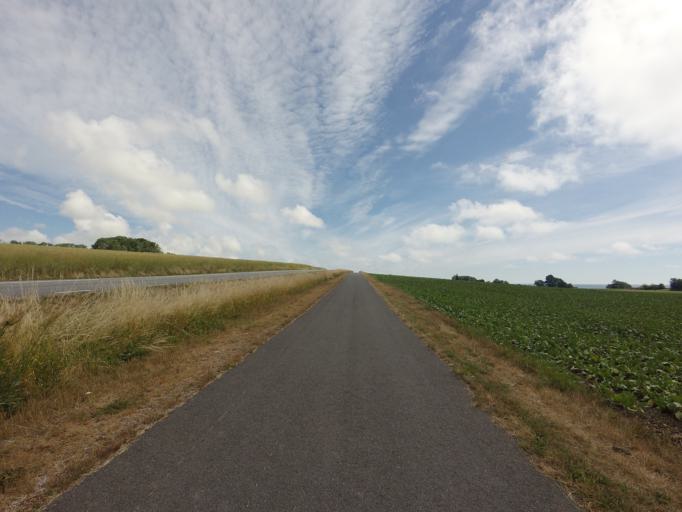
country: SE
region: Skane
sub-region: Simrishamns Kommun
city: Simrishamn
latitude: 55.4913
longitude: 14.3099
